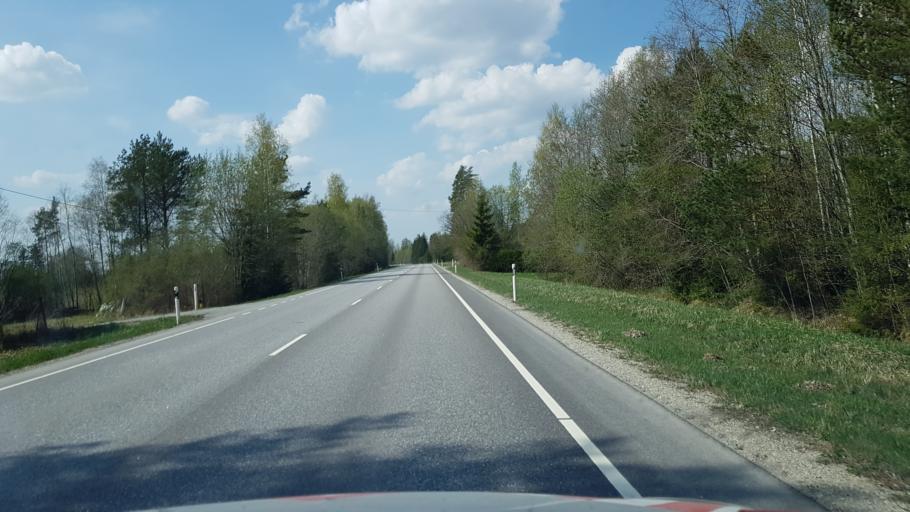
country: EE
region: Paernumaa
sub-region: Vaendra vald (alev)
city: Vandra
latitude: 58.6701
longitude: 25.1346
